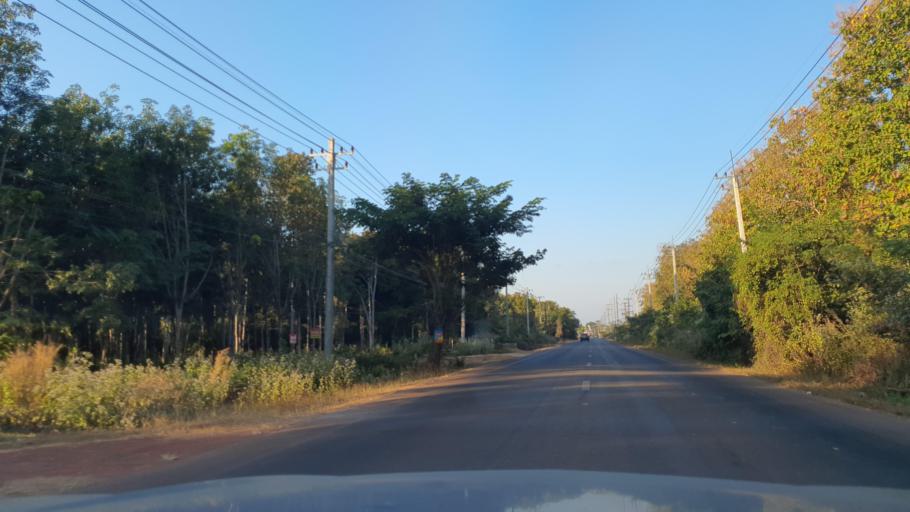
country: TH
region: Nakhon Phanom
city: Si Songkhram
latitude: 17.5767
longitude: 104.2326
